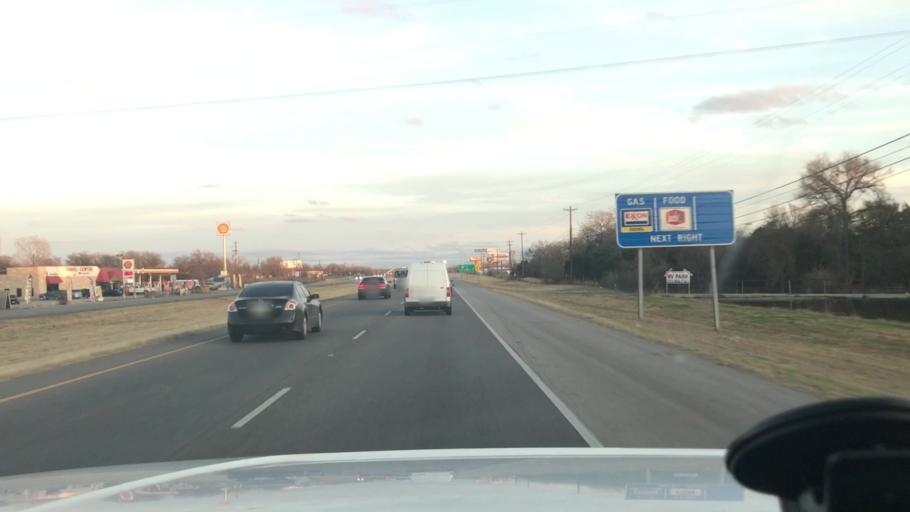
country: US
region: Texas
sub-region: Bastrop County
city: Wyldwood
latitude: 30.1169
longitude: -97.4235
